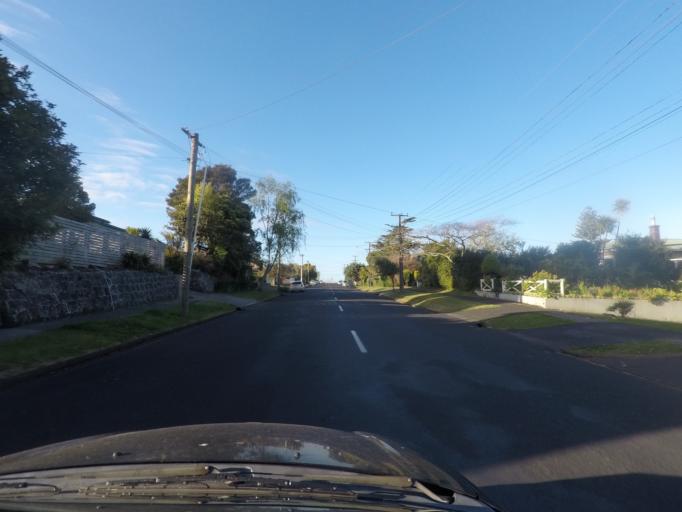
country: NZ
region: Auckland
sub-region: Auckland
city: Waitakere
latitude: -36.9073
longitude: 174.6734
